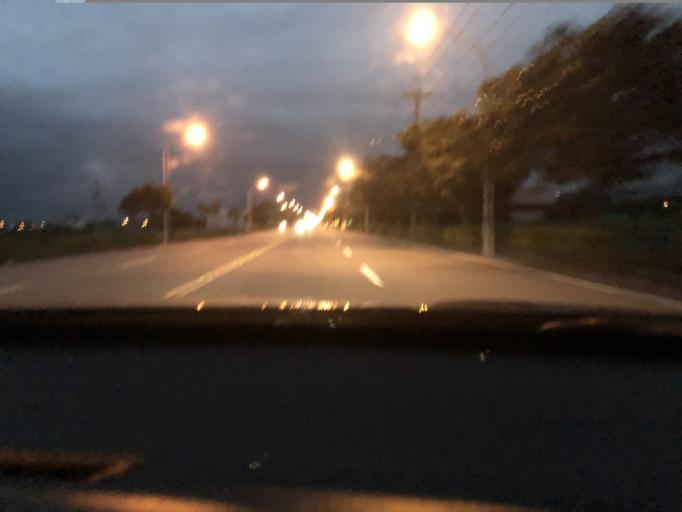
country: TW
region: Taiwan
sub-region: Hualien
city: Hualian
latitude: 23.9492
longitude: 121.5649
